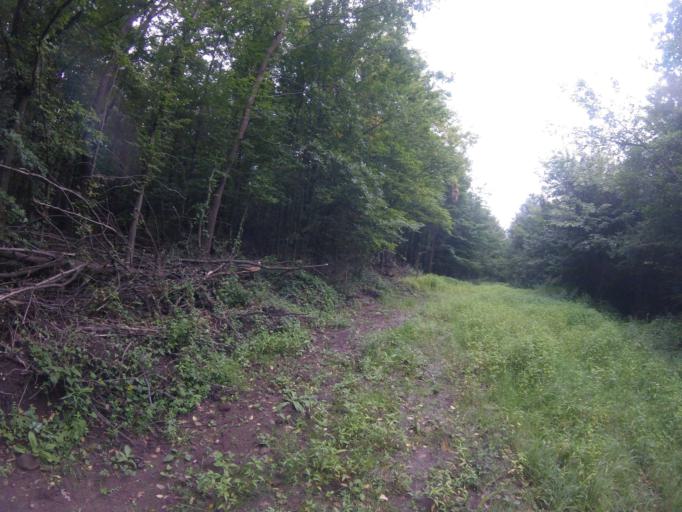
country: SK
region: Nitriansky
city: Sahy
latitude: 48.0293
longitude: 18.9793
